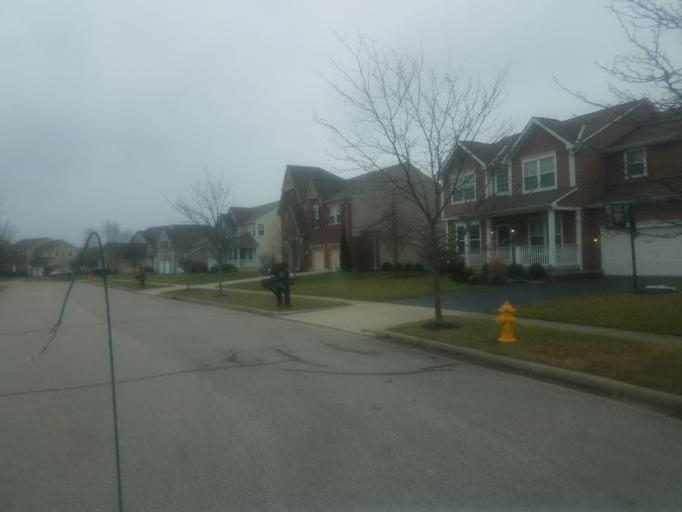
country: US
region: Ohio
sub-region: Franklin County
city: Westerville
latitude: 40.1940
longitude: -82.9219
